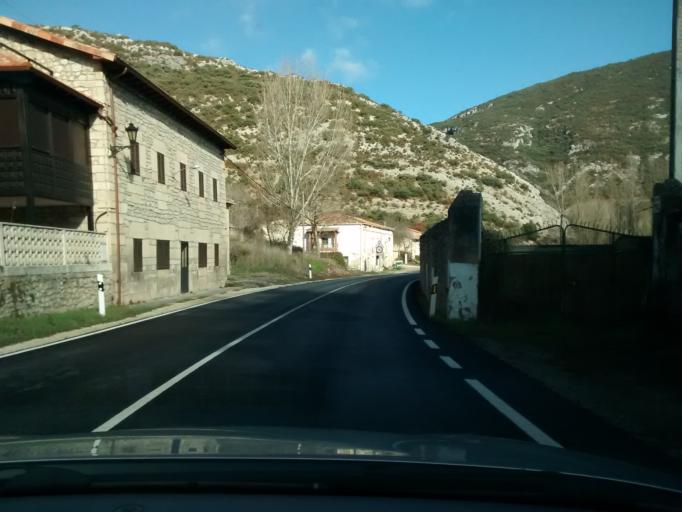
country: ES
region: Castille and Leon
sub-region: Provincia de Burgos
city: Rucandio
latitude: 42.8543
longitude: -3.5957
